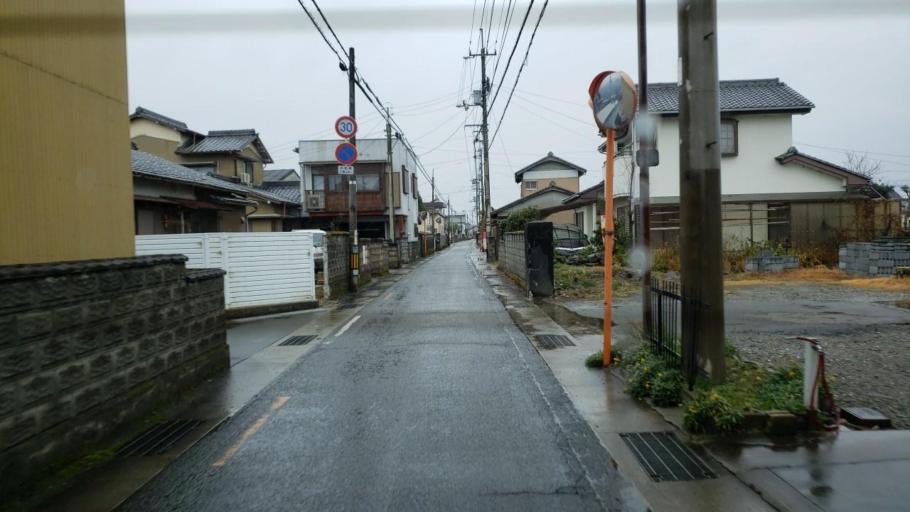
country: JP
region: Tokushima
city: Kamojimacho-jogejima
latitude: 34.0594
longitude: 134.2861
